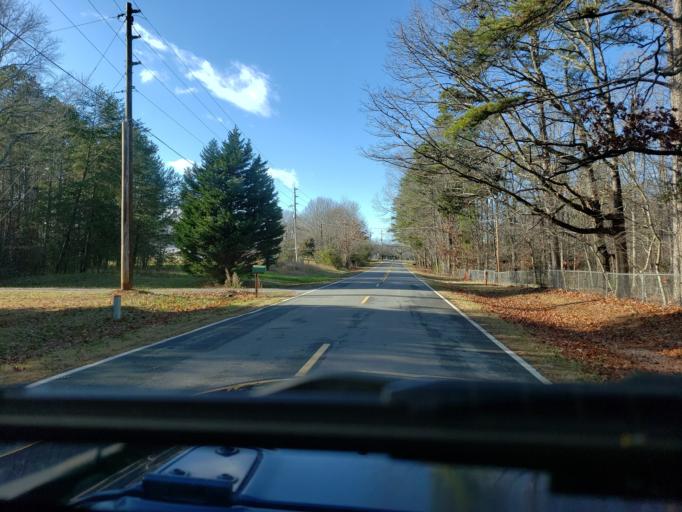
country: US
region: North Carolina
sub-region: Cleveland County
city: Kings Mountain
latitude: 35.1652
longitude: -81.3512
